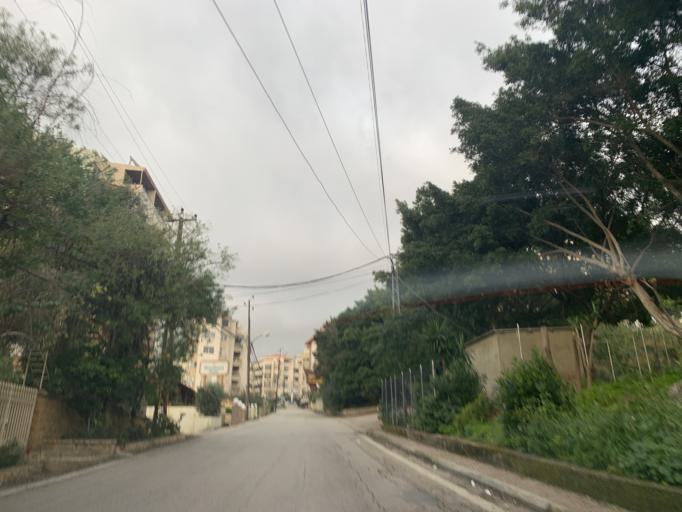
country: LB
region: Mont-Liban
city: Djounie
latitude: 34.0077
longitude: 35.6471
